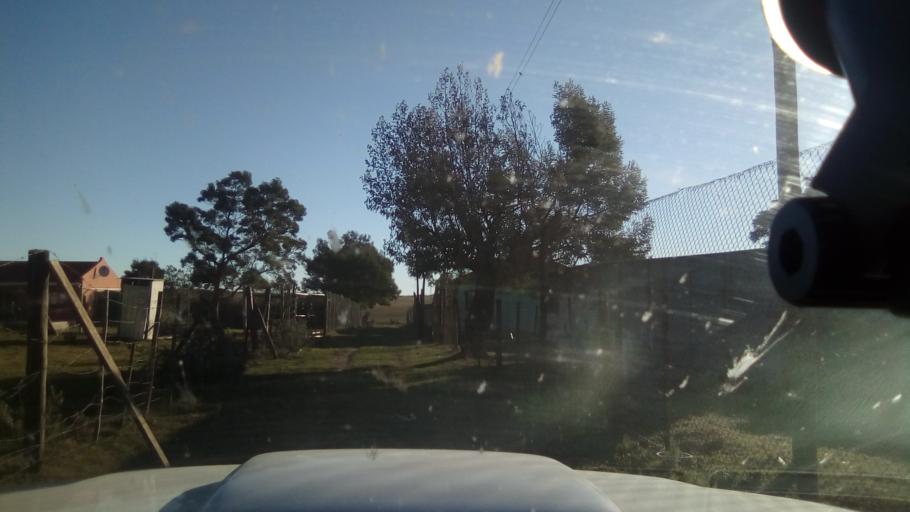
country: ZA
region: Eastern Cape
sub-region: Buffalo City Metropolitan Municipality
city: Bhisho
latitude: -32.9512
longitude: 27.2925
